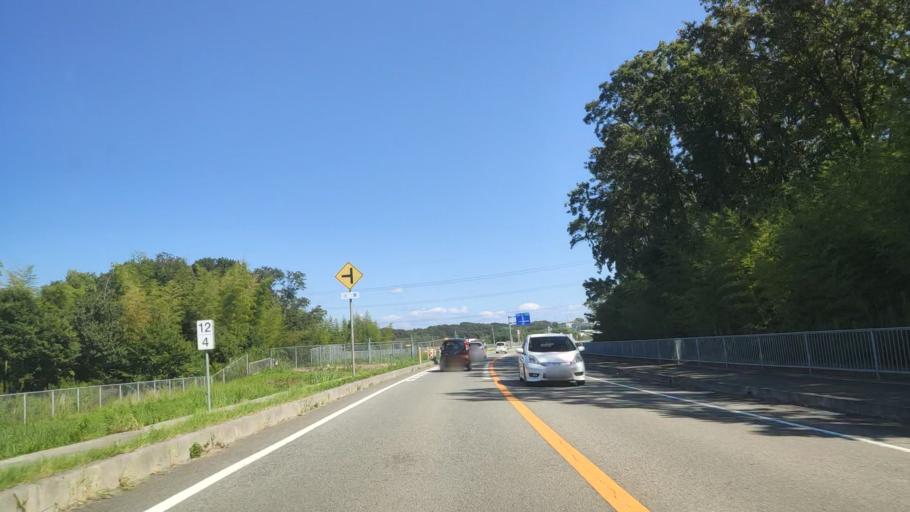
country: JP
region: Hyogo
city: Miki
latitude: 34.7607
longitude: 134.9761
